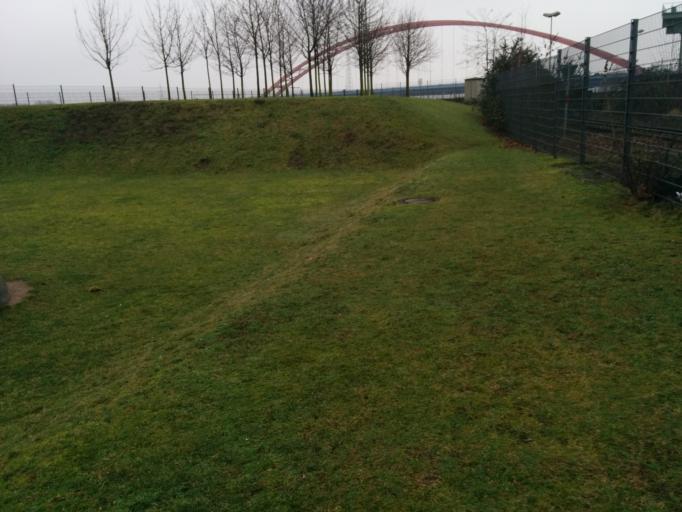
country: DE
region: North Rhine-Westphalia
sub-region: Regierungsbezirk Dusseldorf
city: Hochfeld
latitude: 51.4141
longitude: 6.7436
